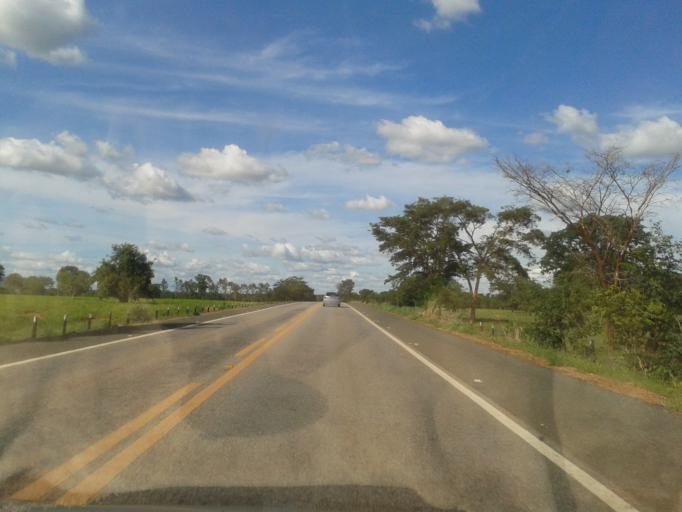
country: BR
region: Goias
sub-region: Mozarlandia
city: Mozarlandia
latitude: -15.0127
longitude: -50.5939
